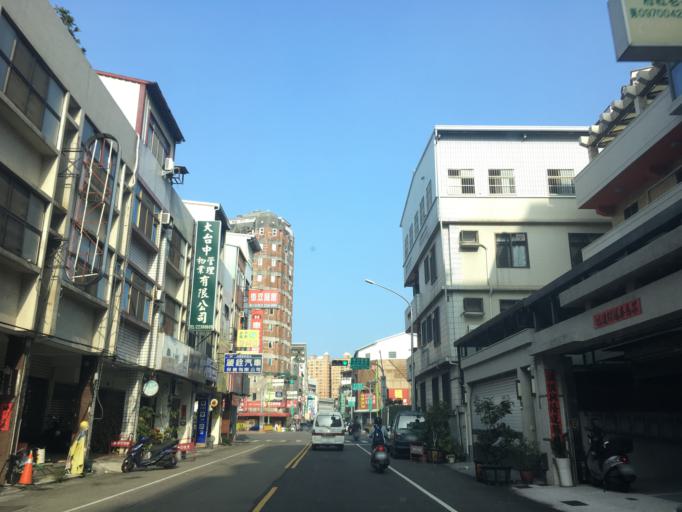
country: TW
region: Taiwan
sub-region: Taichung City
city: Taichung
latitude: 24.1686
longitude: 120.6794
